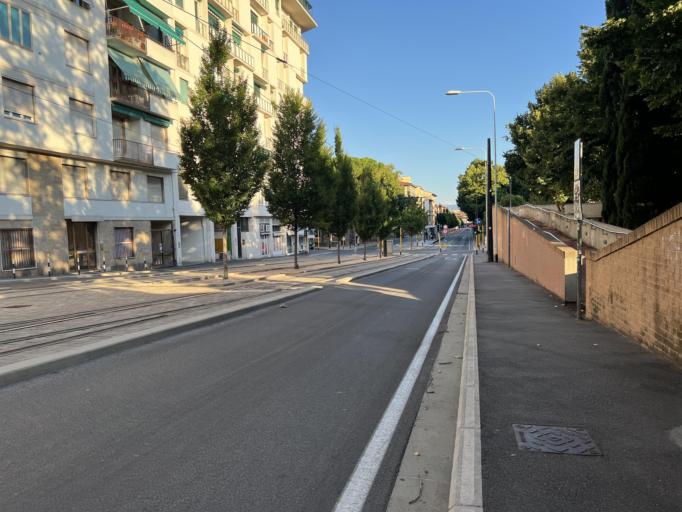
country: IT
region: Tuscany
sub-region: Province of Florence
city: Florence
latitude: 43.7922
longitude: 11.2466
